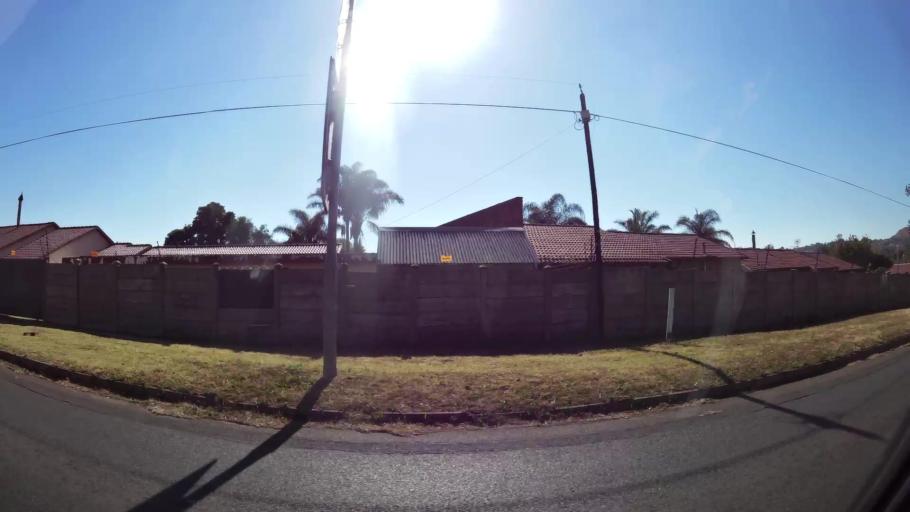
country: ZA
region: Gauteng
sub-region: City of Johannesburg Metropolitan Municipality
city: Roodepoort
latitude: -26.1233
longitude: 27.8660
